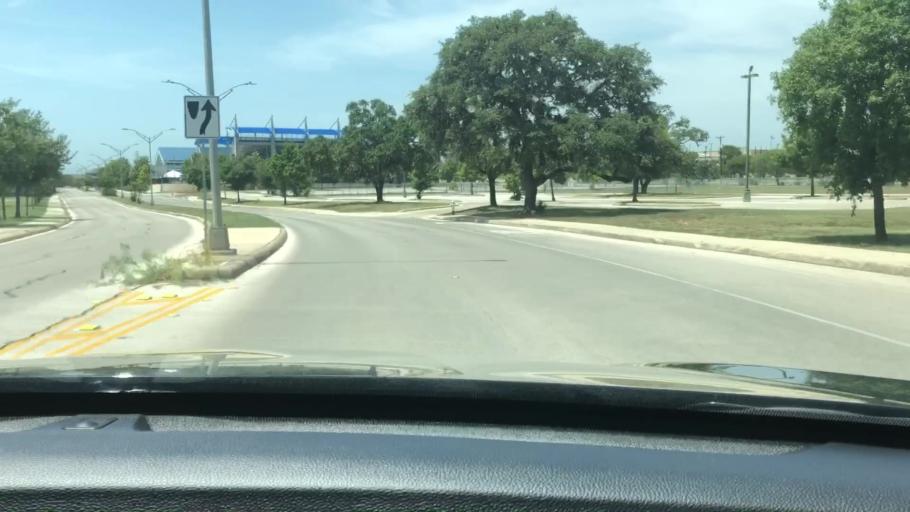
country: US
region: Texas
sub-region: Bexar County
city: Helotes
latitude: 29.5615
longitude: -98.6495
